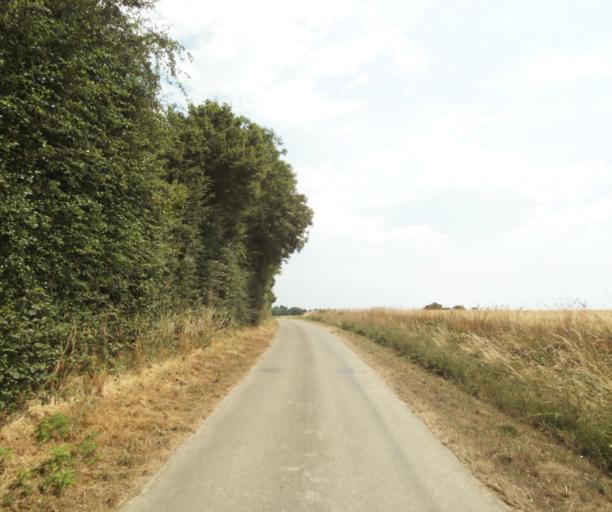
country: FR
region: Centre
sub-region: Departement d'Eure-et-Loir
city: La Bazoche-Gouet
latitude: 48.1848
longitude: 0.9853
